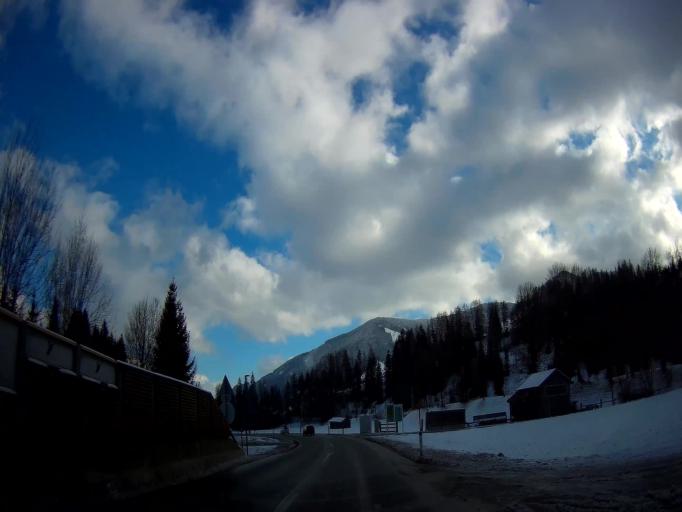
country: AT
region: Salzburg
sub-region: Politischer Bezirk Zell am See
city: Leogang
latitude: 47.4399
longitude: 12.7442
